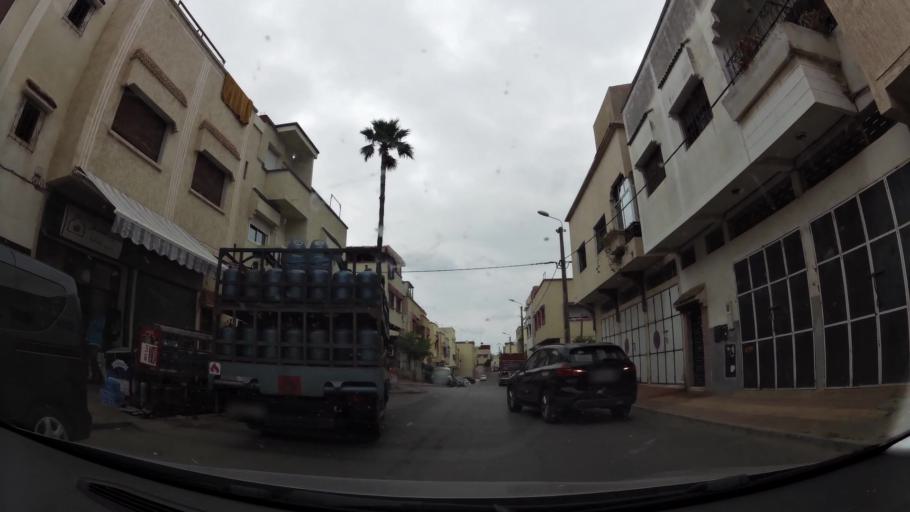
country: MA
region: Rabat-Sale-Zemmour-Zaer
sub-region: Rabat
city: Rabat
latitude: 33.9751
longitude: -6.8136
